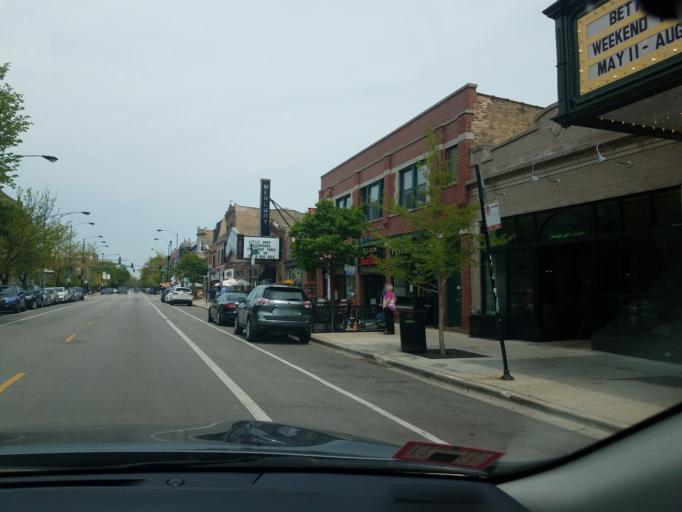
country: US
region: Illinois
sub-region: Cook County
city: Lincolnwood
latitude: 41.9498
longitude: -87.6641
